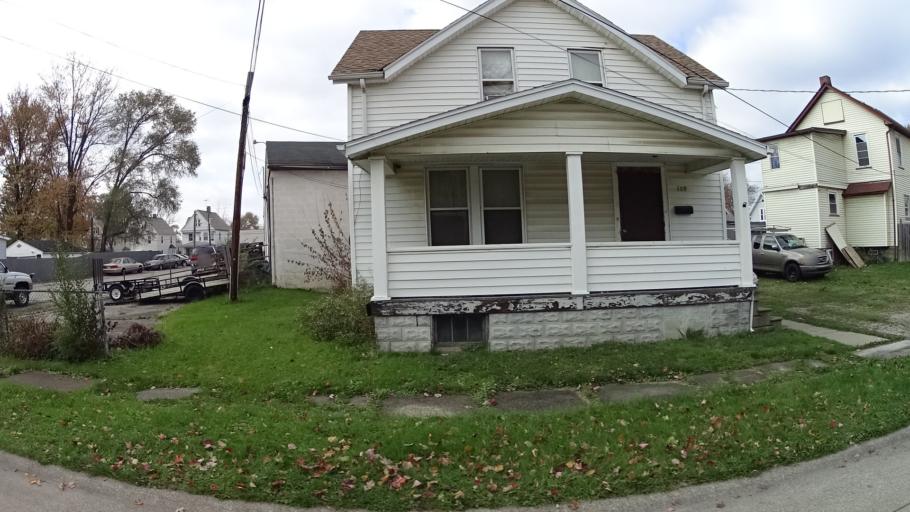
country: US
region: Ohio
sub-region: Lorain County
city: Elyria
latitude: 41.3734
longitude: -82.0899
